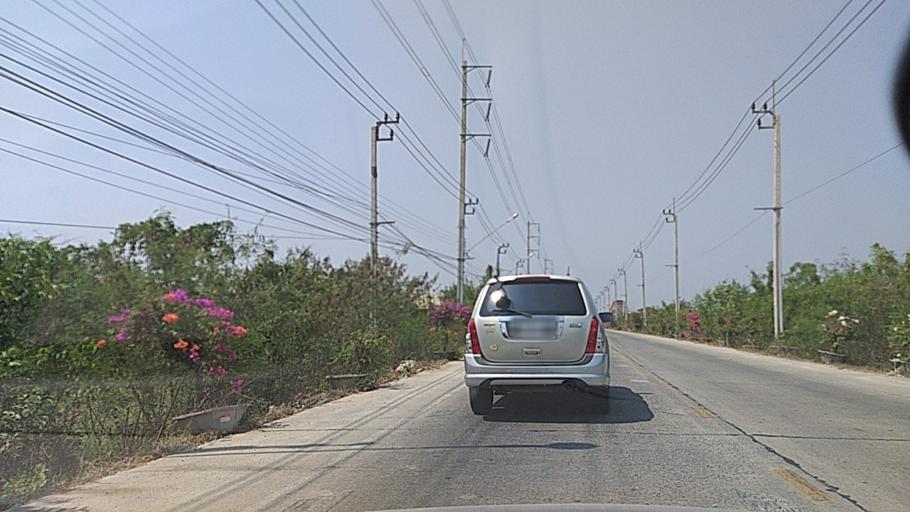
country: TH
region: Nonthaburi
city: Sai Noi
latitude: 13.9690
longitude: 100.3103
